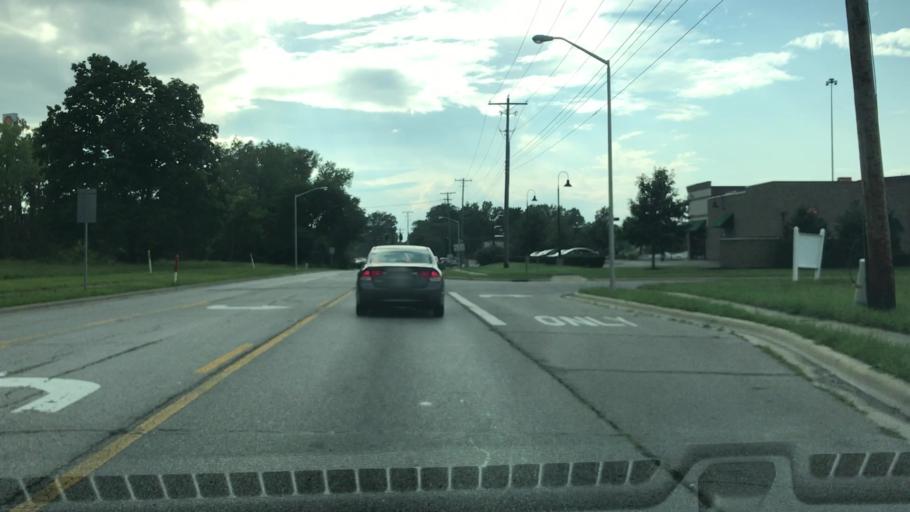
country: US
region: Ohio
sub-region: Franklin County
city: Grove City
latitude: 39.9010
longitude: -83.0754
